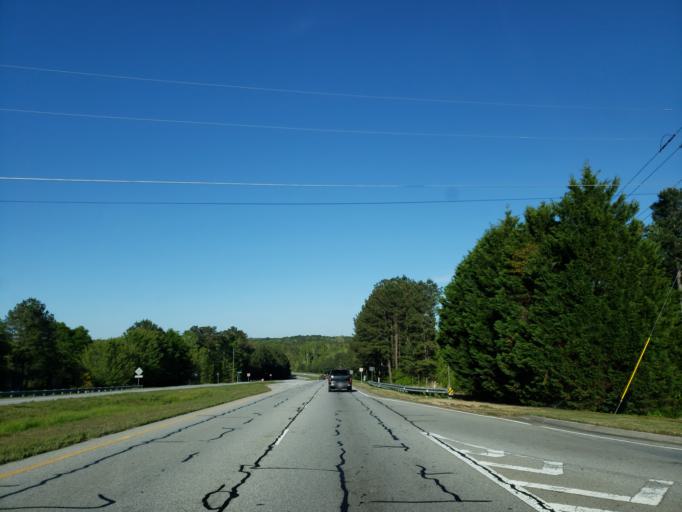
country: US
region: Georgia
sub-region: Paulding County
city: Dallas
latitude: 33.9143
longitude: -84.8853
